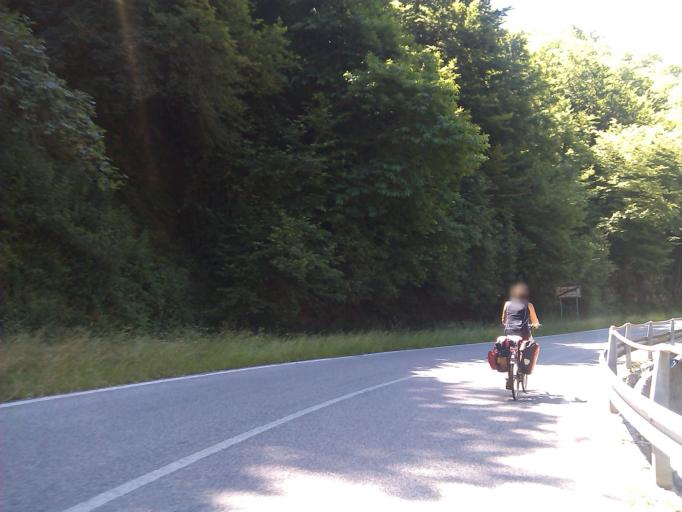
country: IT
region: Tuscany
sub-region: Provincia di Prato
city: Cantagallo
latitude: 44.0490
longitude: 11.0439
